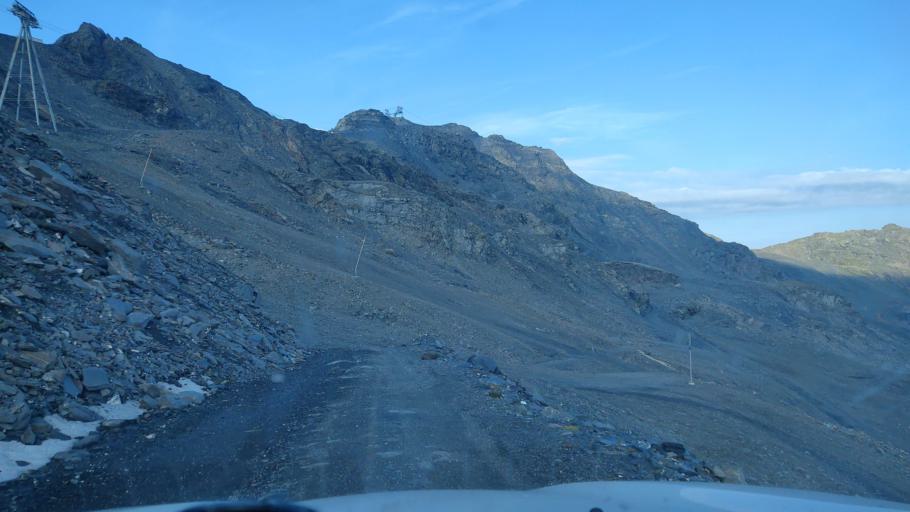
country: FR
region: Rhone-Alpes
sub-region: Departement de la Savoie
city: Val Thorens
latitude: 45.2712
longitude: 6.5806
